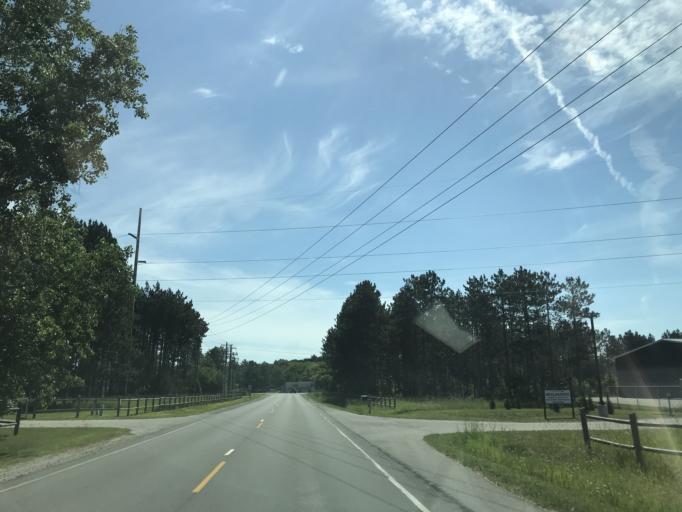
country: US
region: Michigan
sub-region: Grand Traverse County
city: Traverse City
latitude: 44.6541
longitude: -85.6991
